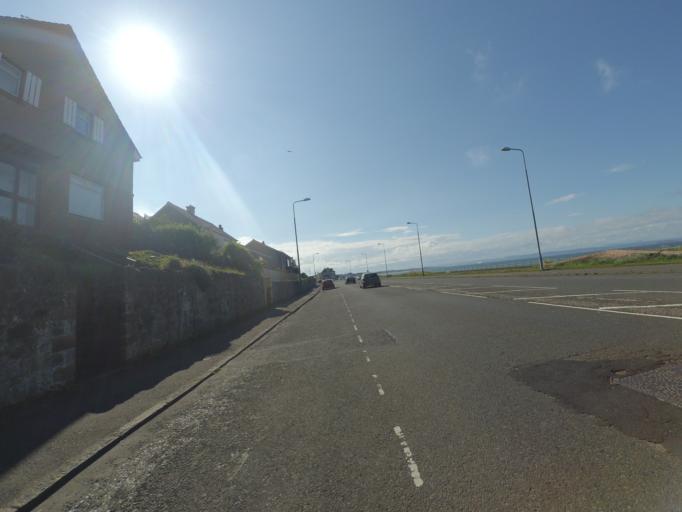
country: GB
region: Scotland
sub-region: East Lothian
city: Musselburgh
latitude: 55.9482
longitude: -3.0842
